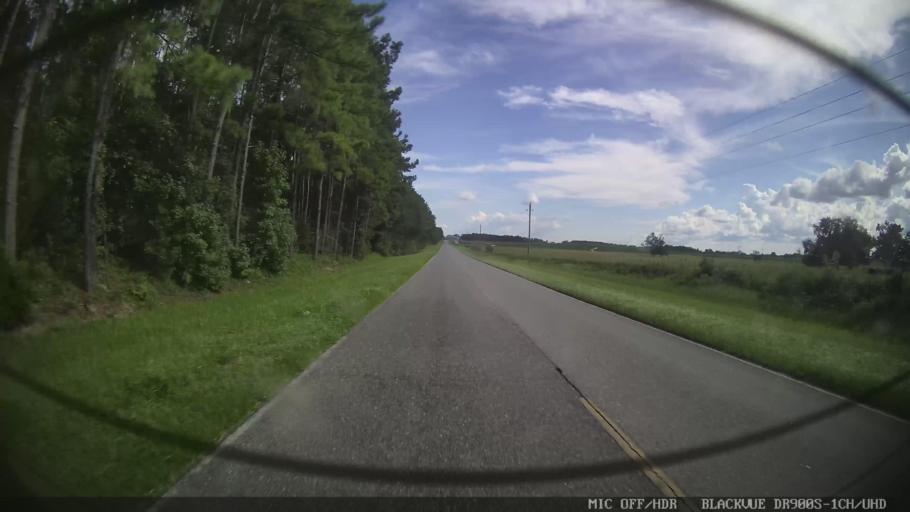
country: US
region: Georgia
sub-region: Echols County
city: Statenville
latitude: 30.5952
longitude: -83.2242
